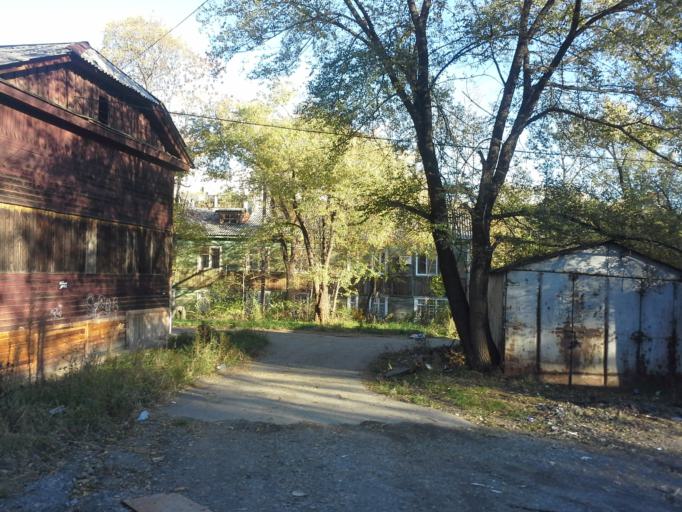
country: RU
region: Khabarovsk Krai
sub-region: Khabarovskiy Rayon
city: Khabarovsk
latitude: 48.4859
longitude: 135.0641
